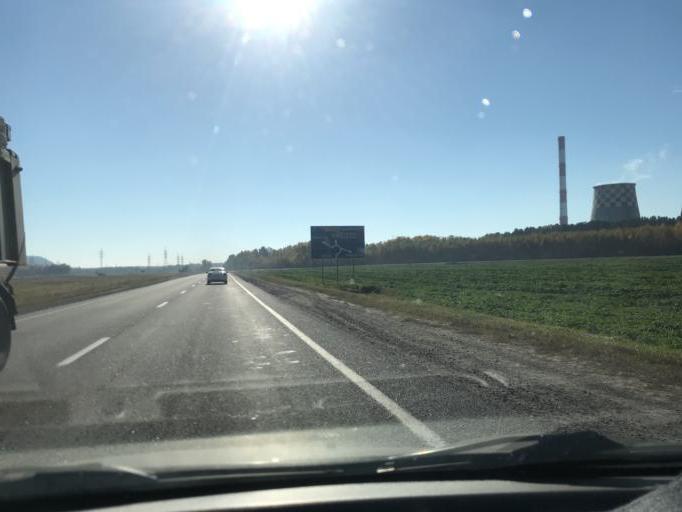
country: BY
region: Gomel
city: Kastsyukowka
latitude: 52.4566
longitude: 30.8248
